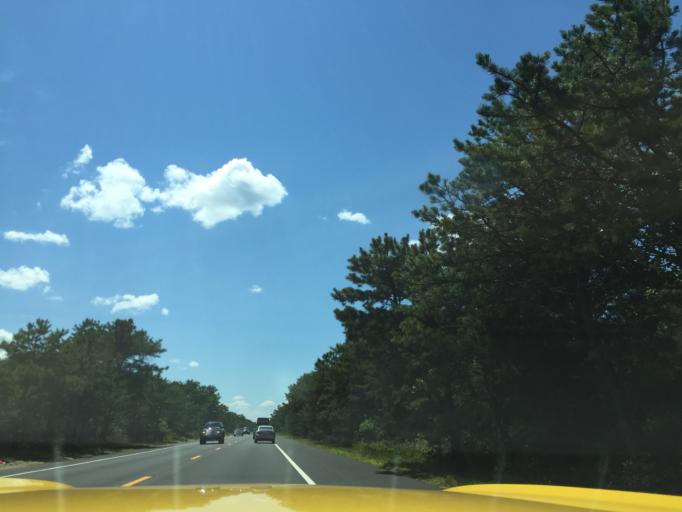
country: US
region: New York
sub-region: Suffolk County
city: Amagansett
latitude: 40.9874
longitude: -72.0840
